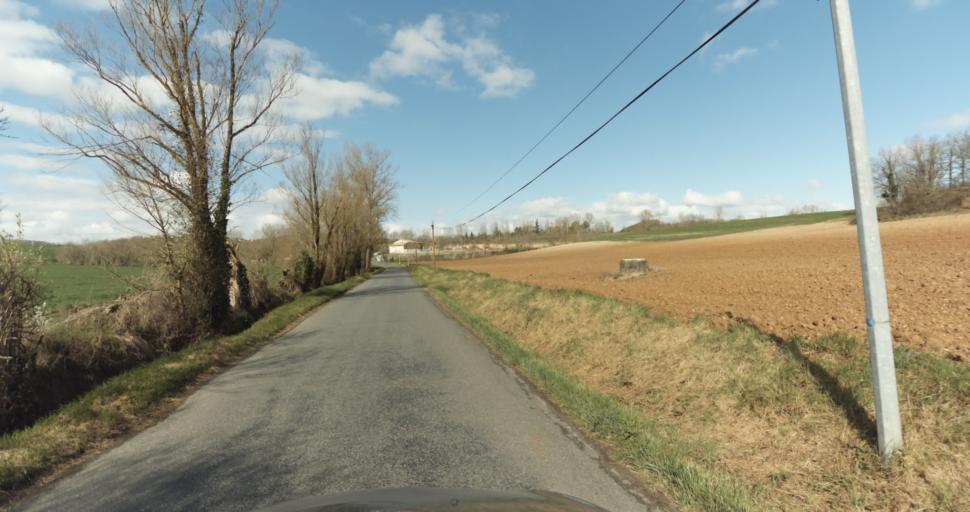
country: FR
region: Midi-Pyrenees
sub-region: Departement du Tarn
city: Frejairolles
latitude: 43.8562
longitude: 2.1927
